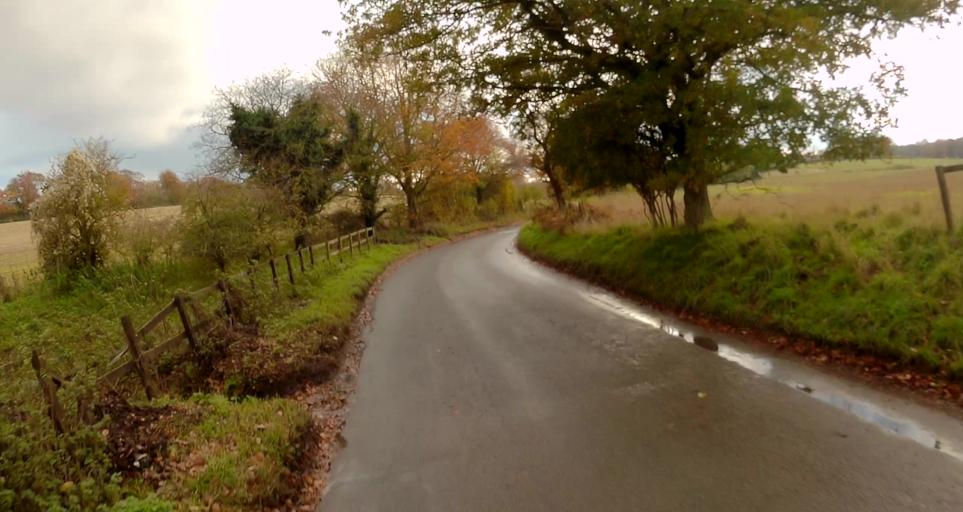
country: GB
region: England
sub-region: Hampshire
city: Old Basing
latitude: 51.2358
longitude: -1.0292
